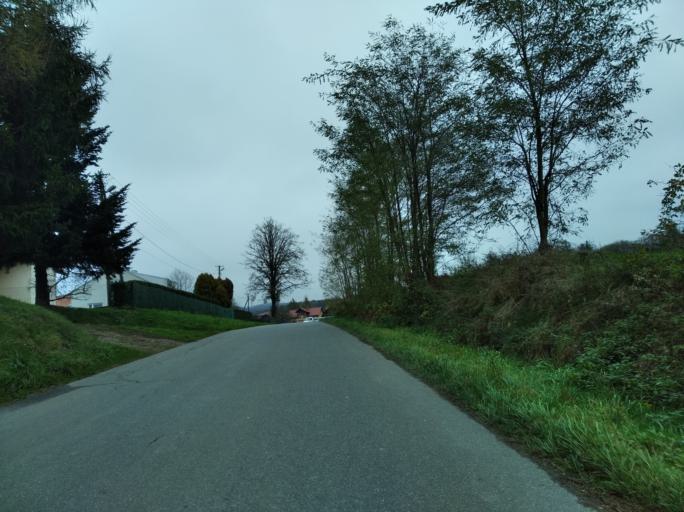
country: PL
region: Subcarpathian Voivodeship
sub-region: Powiat krosnienski
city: Leki
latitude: 49.8010
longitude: 21.6699
